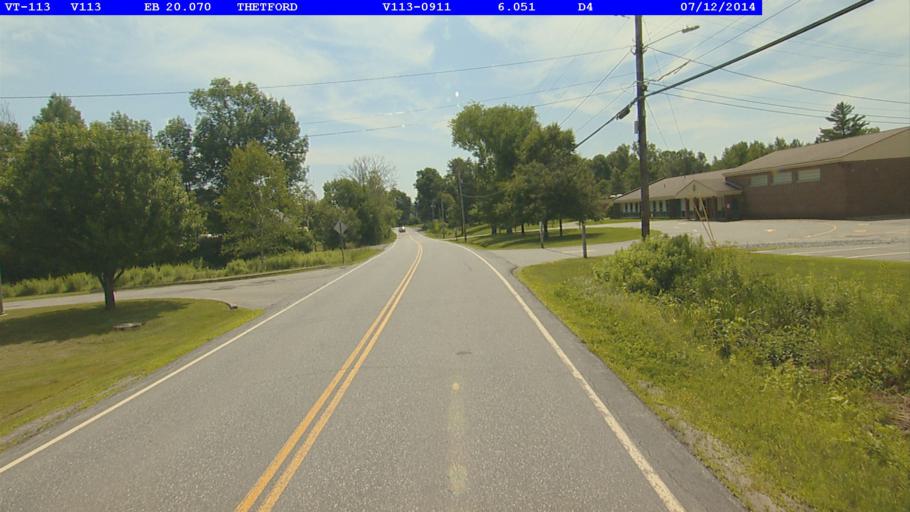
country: US
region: New Hampshire
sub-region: Grafton County
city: Lyme
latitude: 43.8203
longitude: -72.2323
